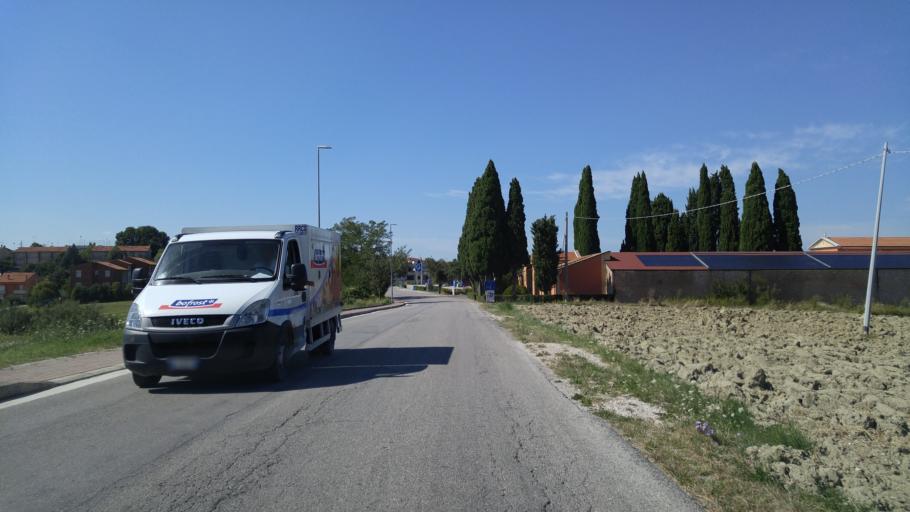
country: IT
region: The Marches
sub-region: Provincia di Pesaro e Urbino
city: San Giorgio di Pesaro
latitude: 43.7141
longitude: 12.9852
